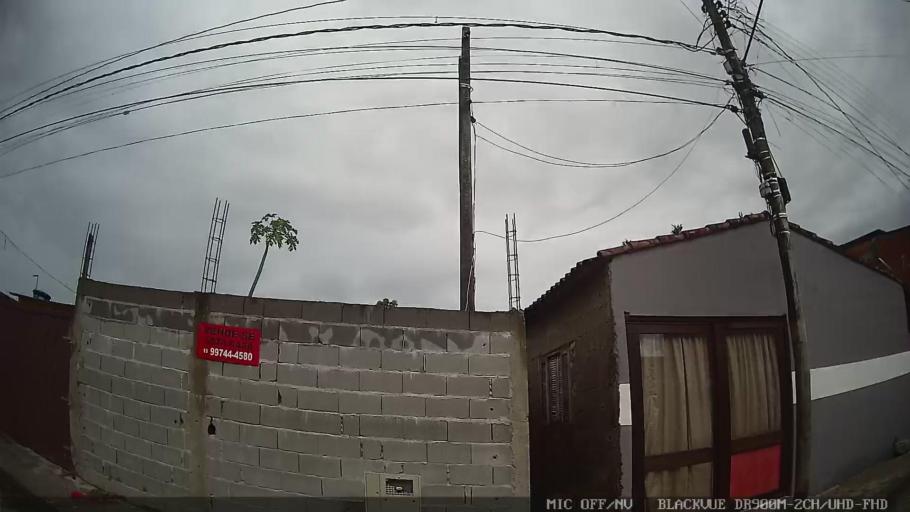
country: BR
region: Sao Paulo
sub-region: Itanhaem
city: Itanhaem
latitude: -24.1590
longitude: -46.7991
